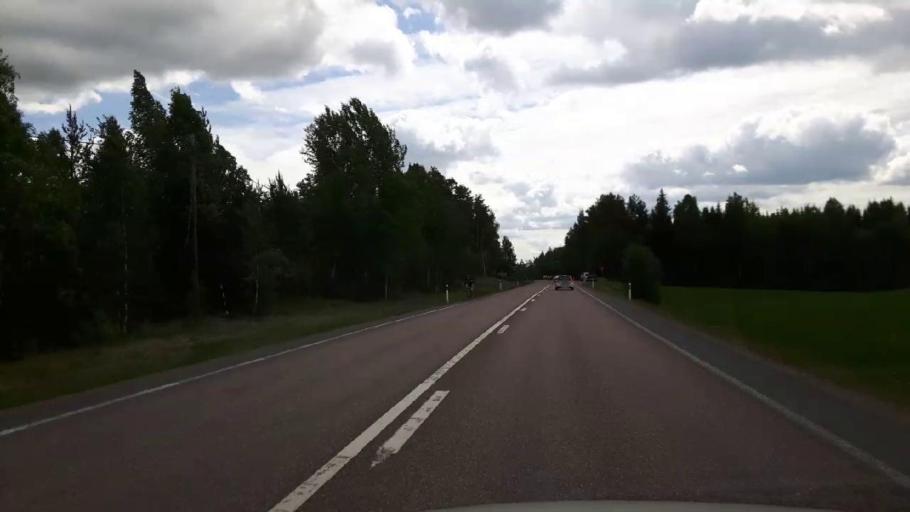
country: SE
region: Dalarna
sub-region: Saters Kommun
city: Saeter
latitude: 60.4680
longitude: 15.7979
